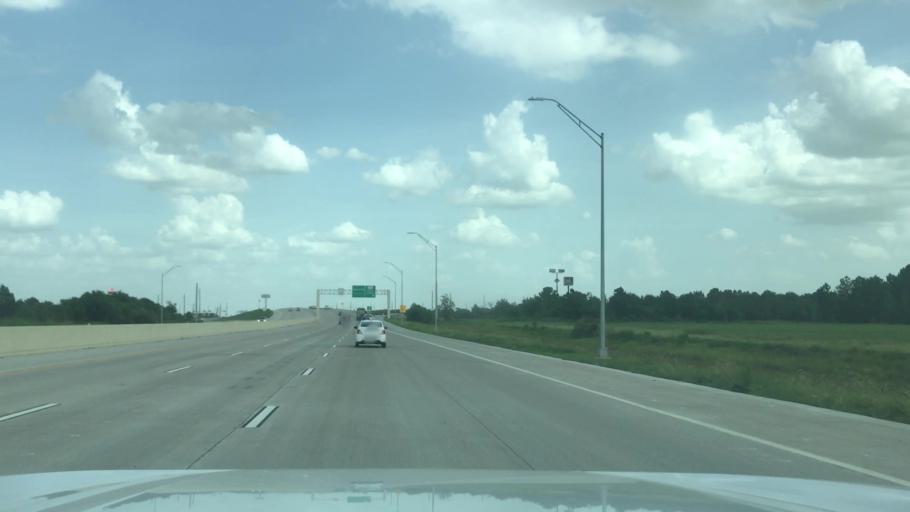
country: US
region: Texas
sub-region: Waller County
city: Waller
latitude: 30.0659
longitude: -95.9154
